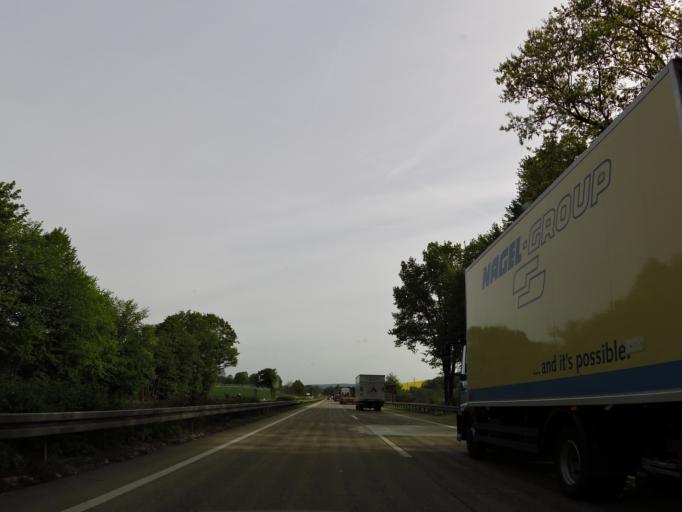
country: DE
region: Lower Saxony
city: Gittelde
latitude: 51.8282
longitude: 10.1134
